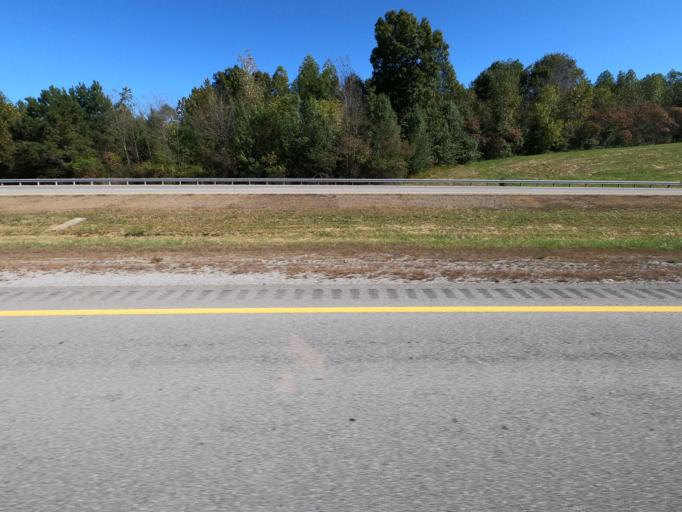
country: US
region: Tennessee
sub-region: Williamson County
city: Fairview
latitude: 35.8794
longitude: -87.0992
